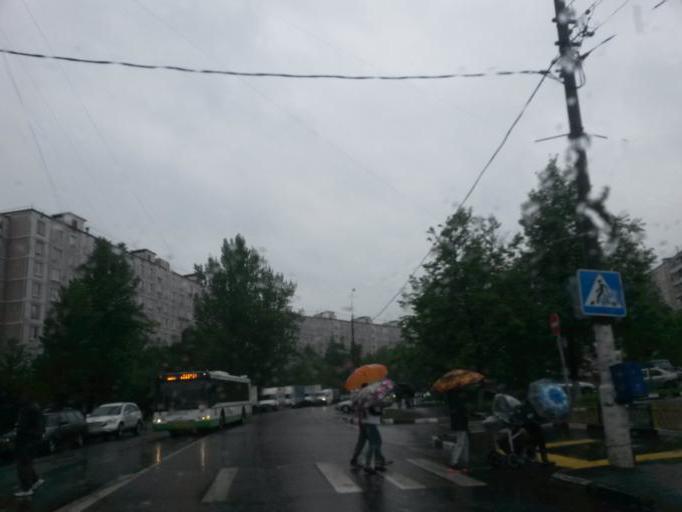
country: RU
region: Moscow
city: Zyablikovo
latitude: 55.6195
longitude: 37.7534
